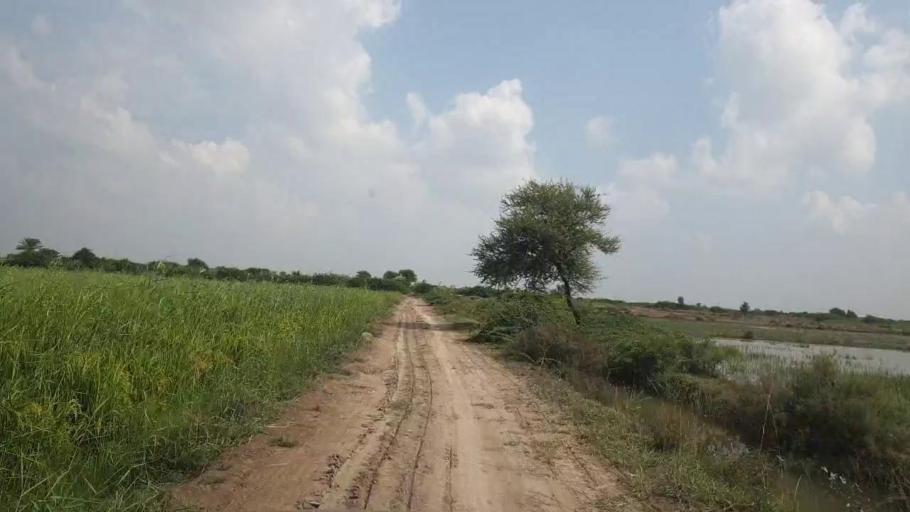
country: PK
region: Sindh
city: Badin
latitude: 24.5328
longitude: 68.6403
